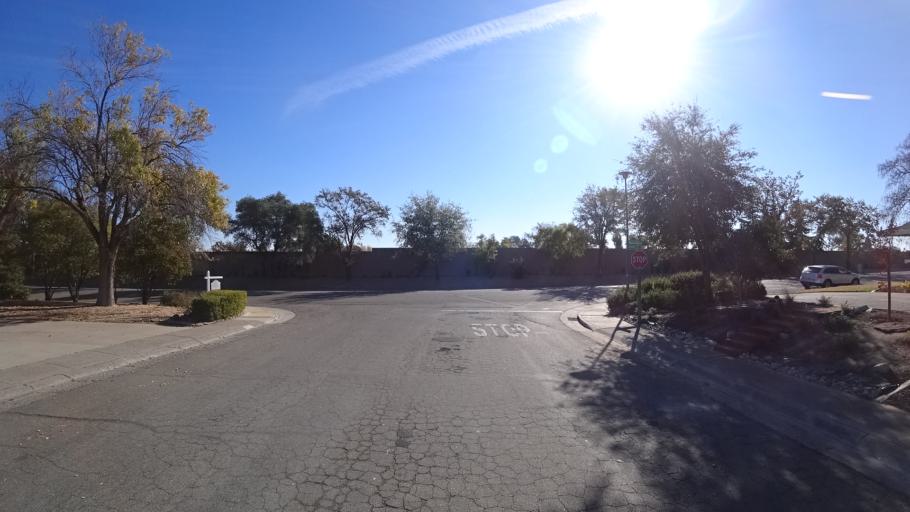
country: US
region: California
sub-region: Sacramento County
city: Antelope
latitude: 38.7113
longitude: -121.3065
